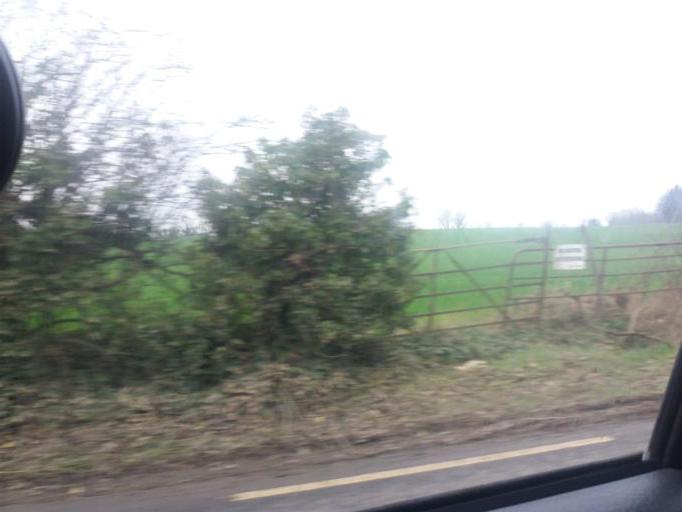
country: IE
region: Leinster
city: Donaghmede
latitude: 53.4240
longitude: -6.1639
